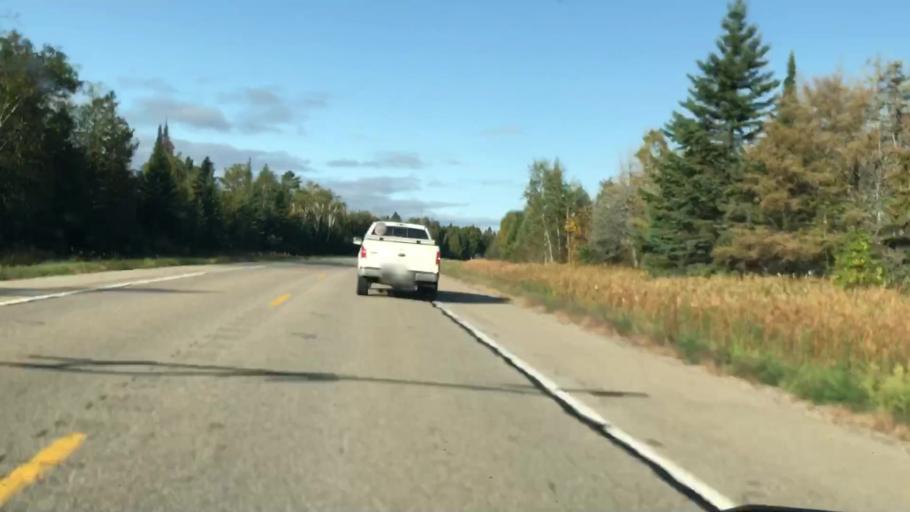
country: US
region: Michigan
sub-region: Luce County
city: Newberry
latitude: 46.3040
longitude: -85.2253
